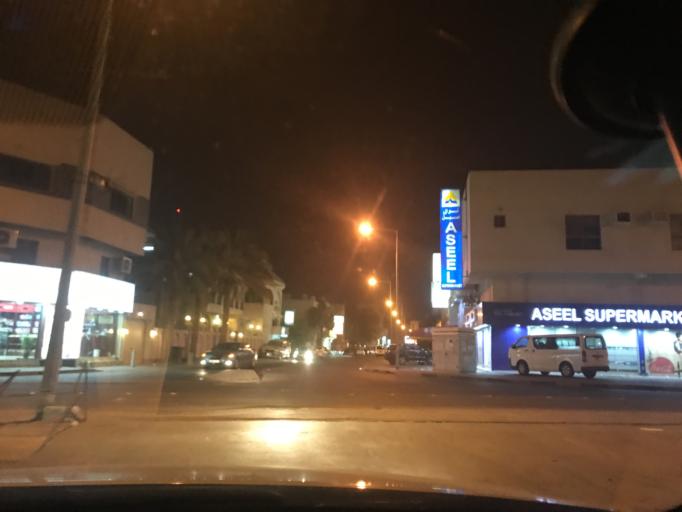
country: BH
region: Muharraq
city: Al Hadd
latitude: 26.2710
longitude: 50.6561
